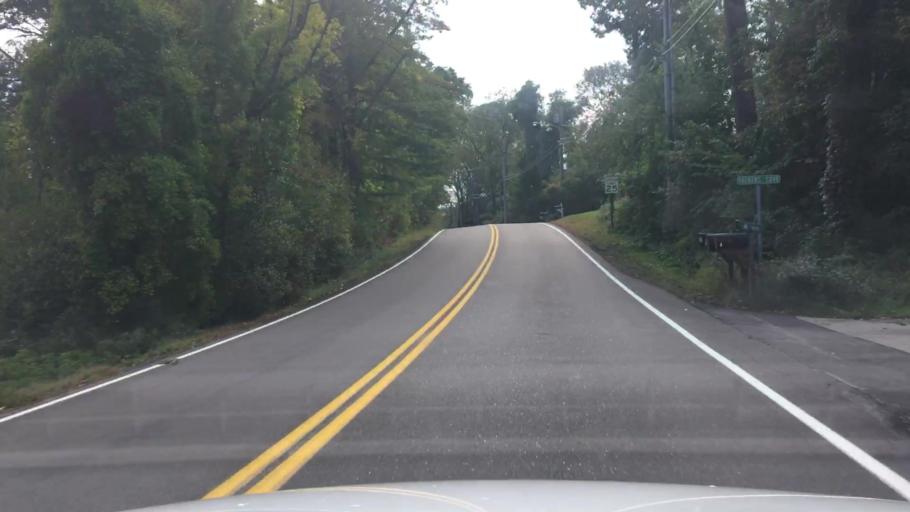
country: US
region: Maine
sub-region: York County
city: Kittery Point
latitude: 43.0947
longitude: -70.7062
